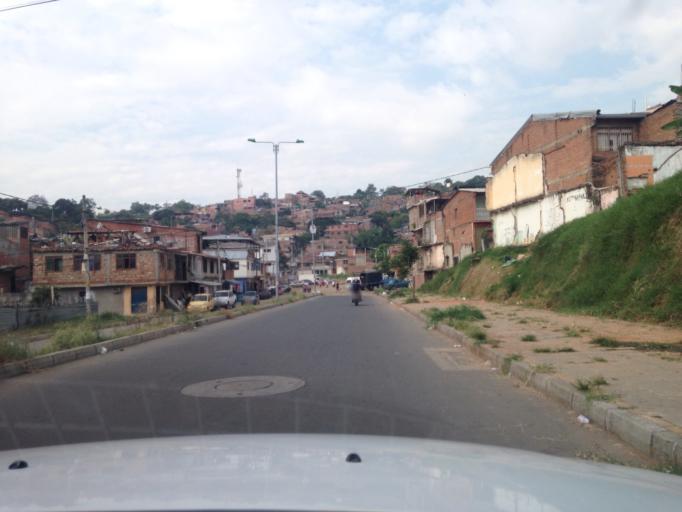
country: CO
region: Valle del Cauca
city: Cali
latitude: 3.3880
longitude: -76.5559
